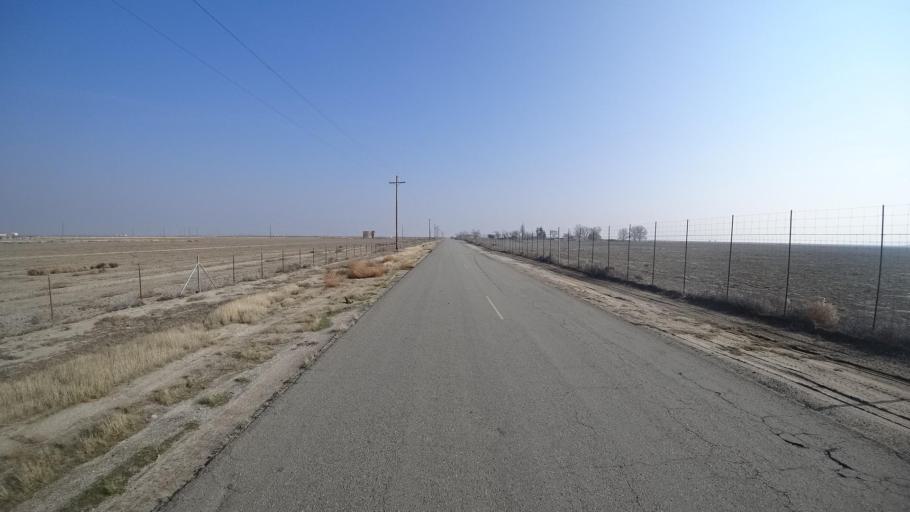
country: US
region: California
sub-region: Kern County
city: Buttonwillow
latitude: 35.3337
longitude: -119.3679
